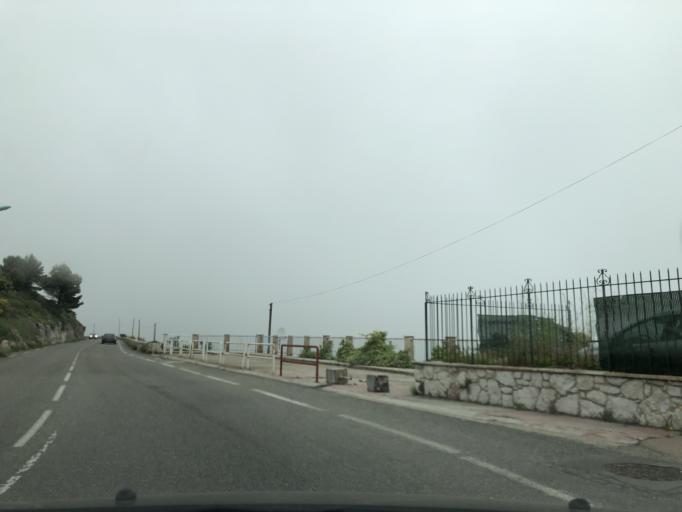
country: FR
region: Provence-Alpes-Cote d'Azur
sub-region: Departement des Alpes-Maritimes
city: Beaulieu-sur-Mer
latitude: 43.7263
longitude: 7.3436
